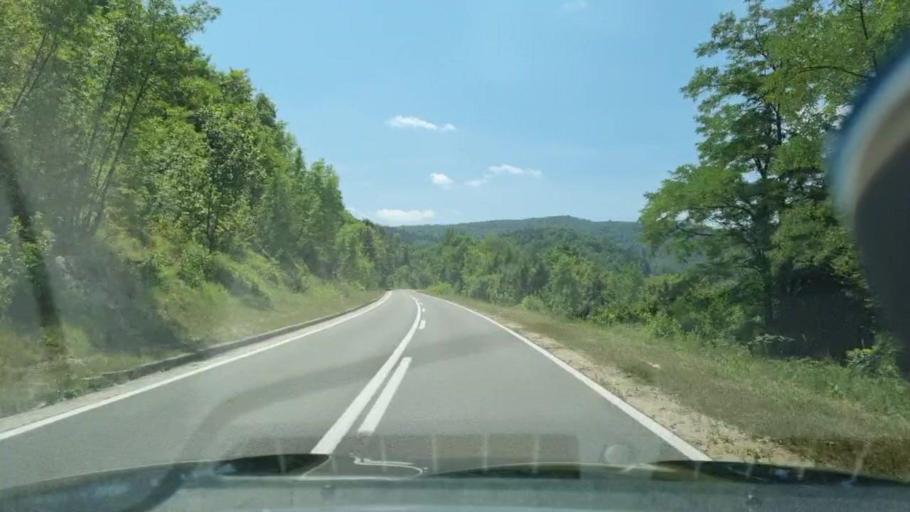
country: BA
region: Federation of Bosnia and Herzegovina
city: Velagici
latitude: 44.5546
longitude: 16.7063
